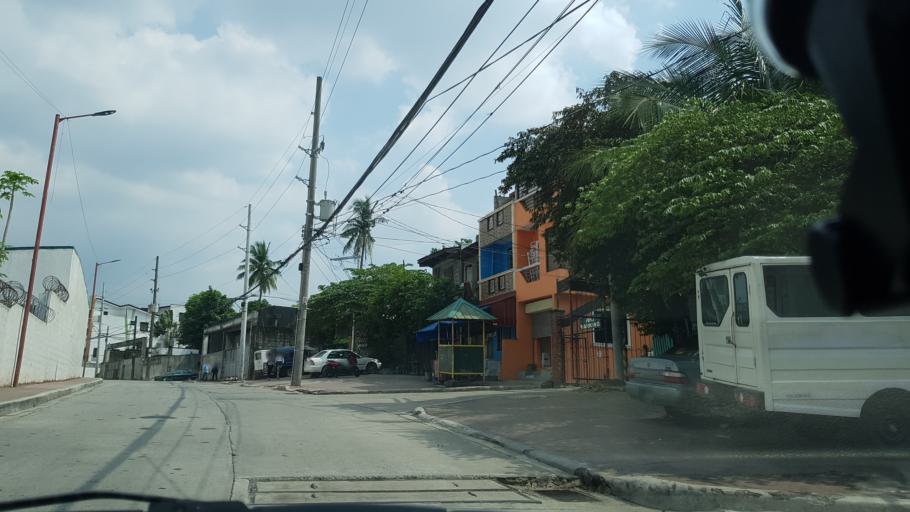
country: PH
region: Calabarzon
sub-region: Province of Rizal
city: San Mateo
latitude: 14.6626
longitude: 121.1261
